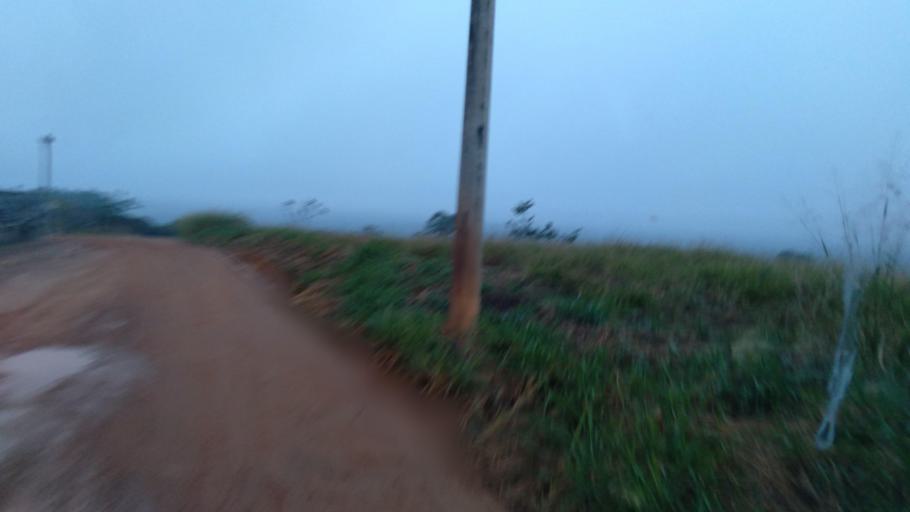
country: BR
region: Goias
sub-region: Mineiros
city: Mineiros
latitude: -17.5821
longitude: -52.5416
